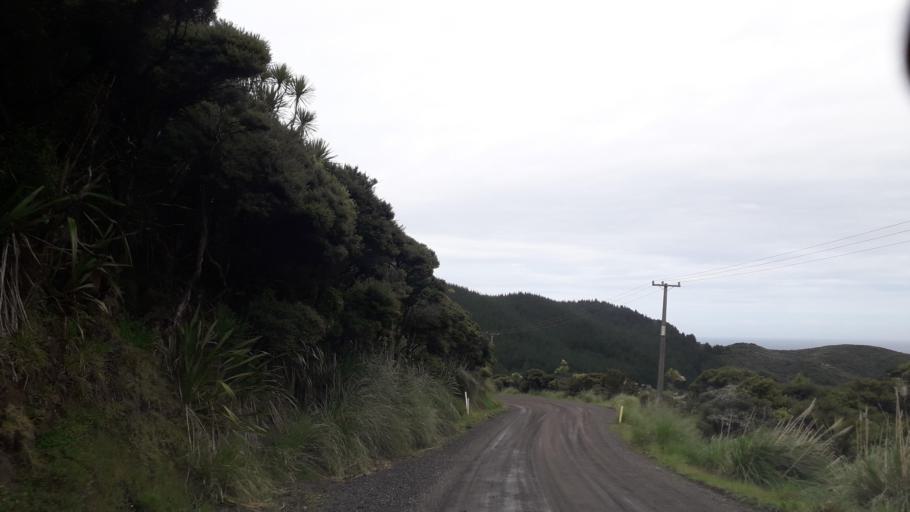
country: NZ
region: Northland
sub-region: Far North District
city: Ahipara
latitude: -35.4384
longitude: 173.3046
